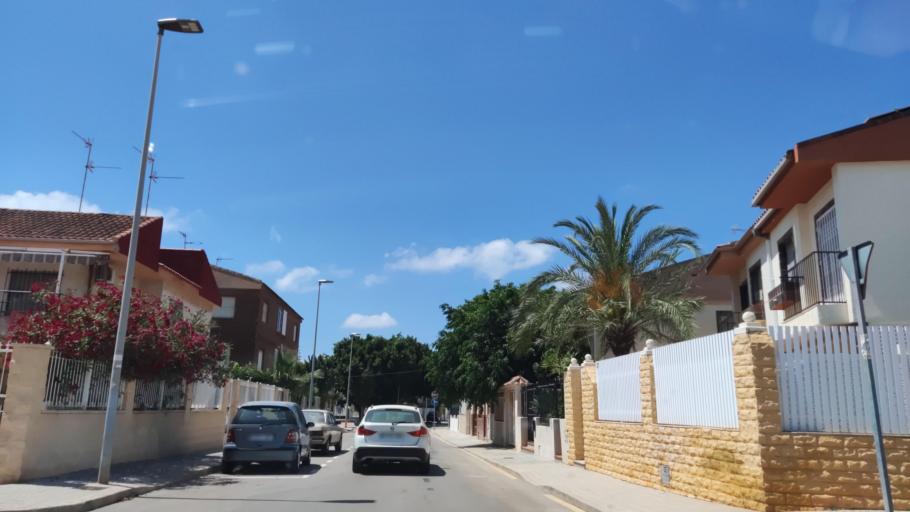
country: ES
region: Murcia
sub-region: Murcia
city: Los Alcazares
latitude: 37.7567
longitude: -0.8367
